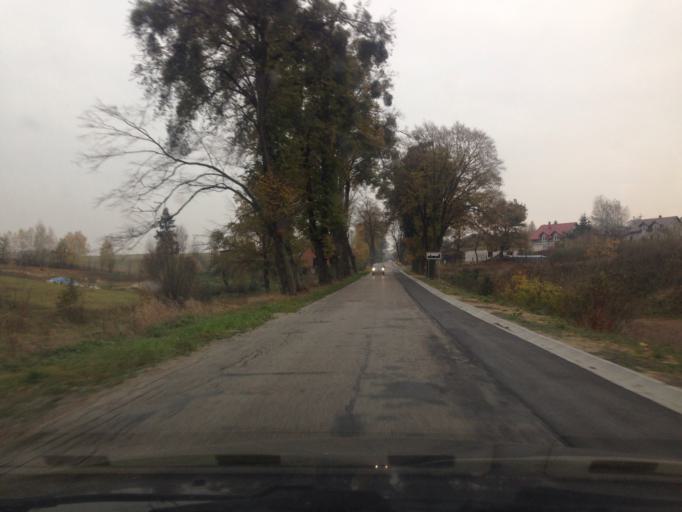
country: PL
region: Kujawsko-Pomorskie
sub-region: Powiat brodnicki
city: Bartniczka
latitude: 53.2323
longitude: 19.6288
